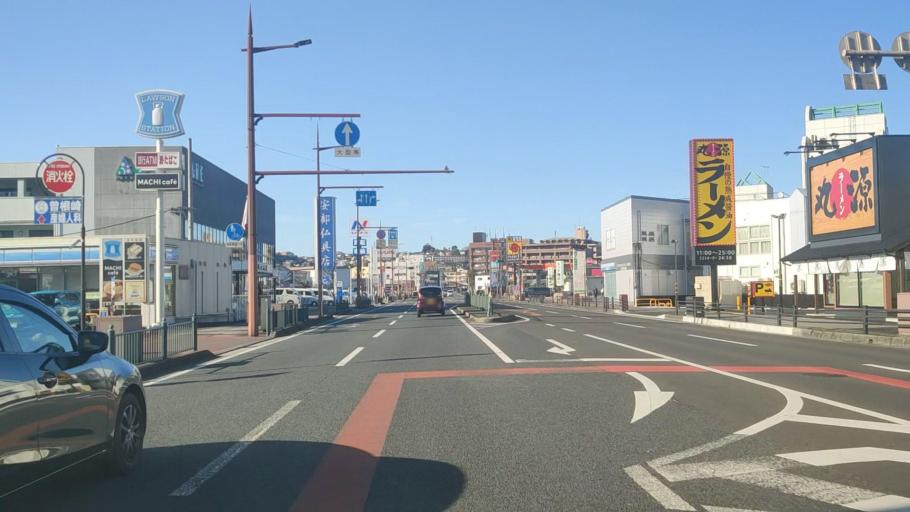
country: JP
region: Oita
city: Oita
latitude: 33.2096
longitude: 131.5993
